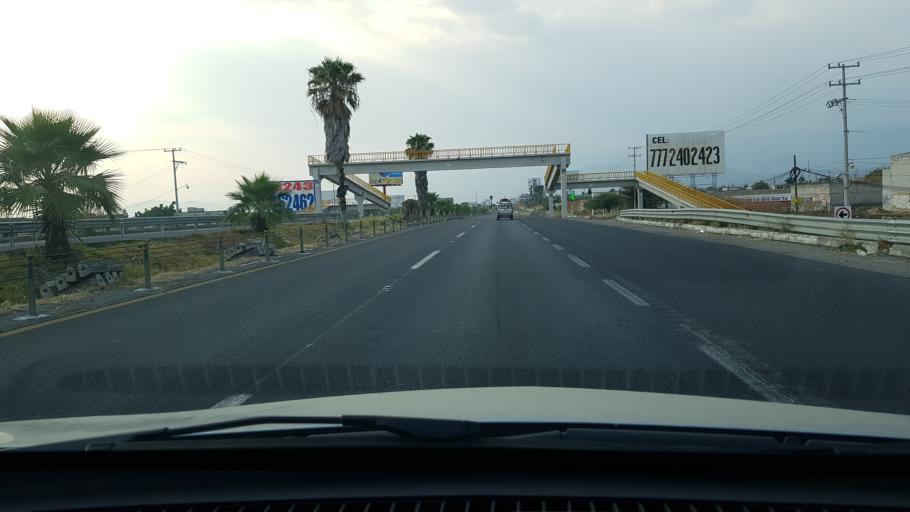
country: MX
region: Morelos
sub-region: Cuautla
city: Tierra Larga (Campo Nuevo)
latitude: 18.8558
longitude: -98.9412
